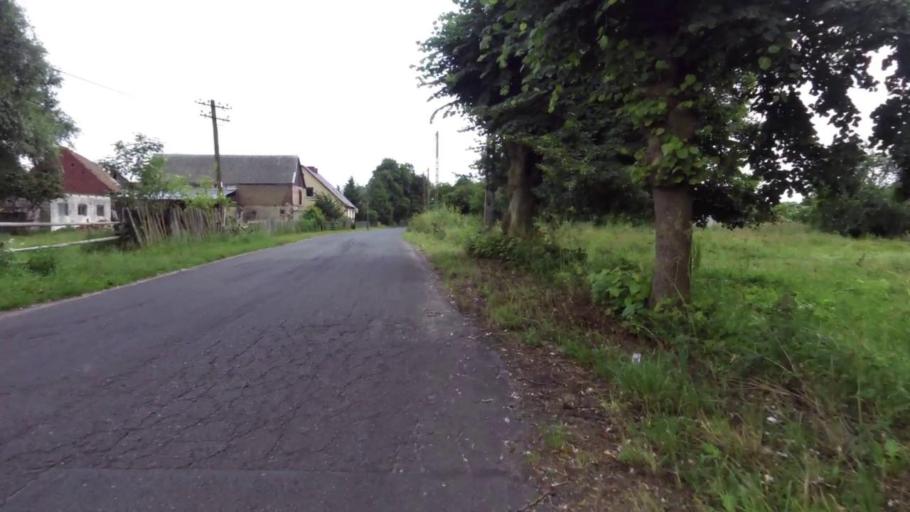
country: PL
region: West Pomeranian Voivodeship
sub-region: Powiat goleniowski
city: Stepnica
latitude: 53.6604
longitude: 14.6109
